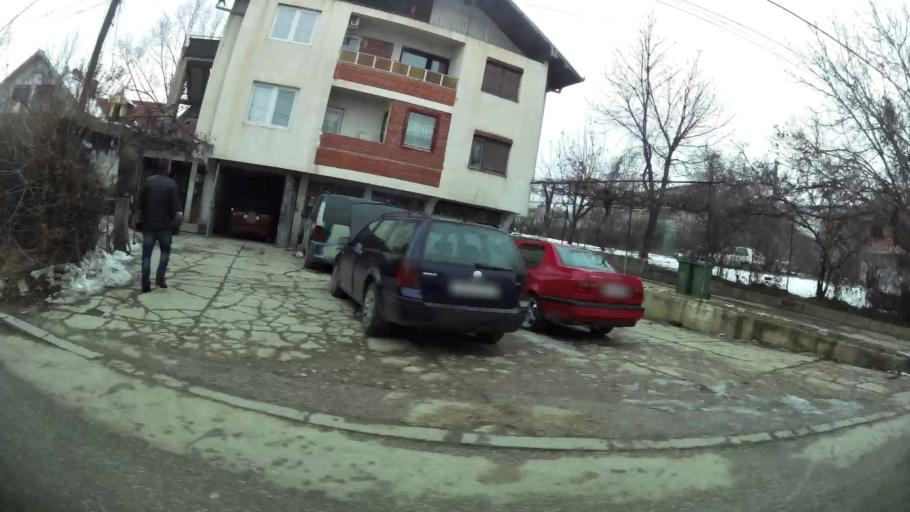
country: MK
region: Suto Orizari
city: Suto Orizare
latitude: 42.0341
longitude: 21.4252
